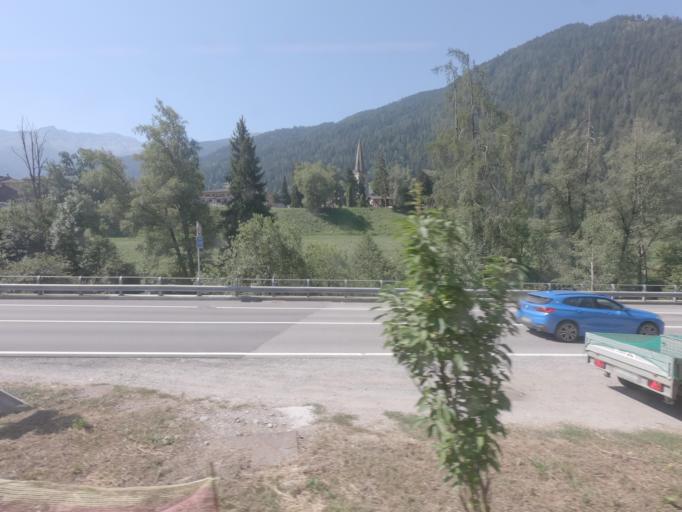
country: CH
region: Valais
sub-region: Entremont District
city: Bagnes
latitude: 46.0821
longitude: 7.2102
